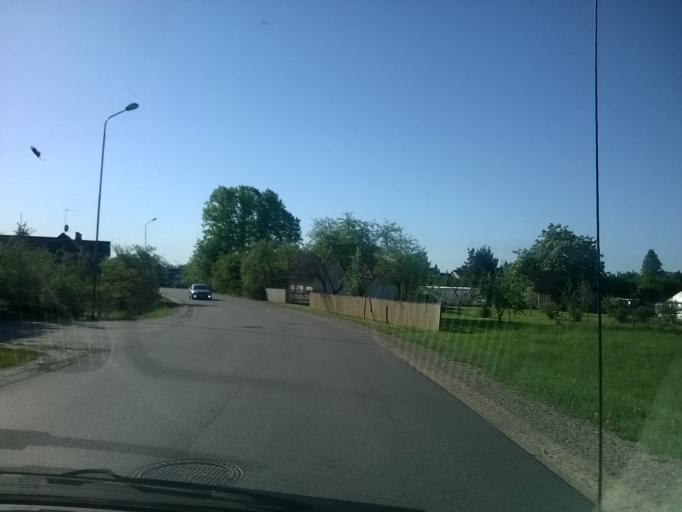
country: LV
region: Valkas Rajons
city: Valka
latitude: 57.7675
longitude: 26.0018
